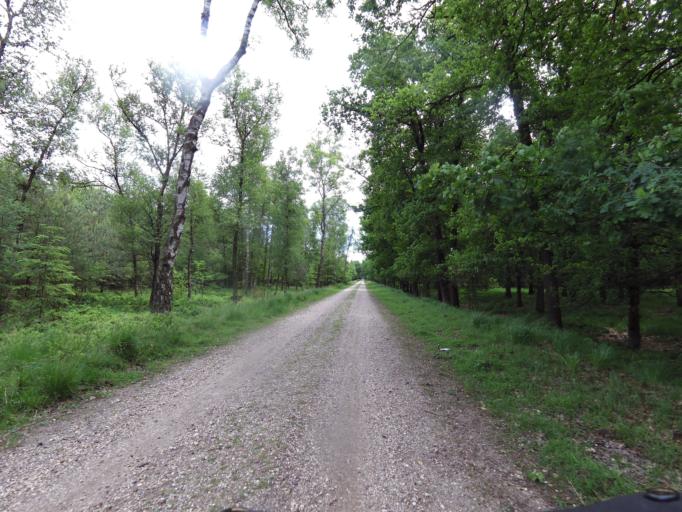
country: NL
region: Gelderland
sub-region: Gemeente Apeldoorn
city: Uddel
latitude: 52.2679
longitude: 5.8266
